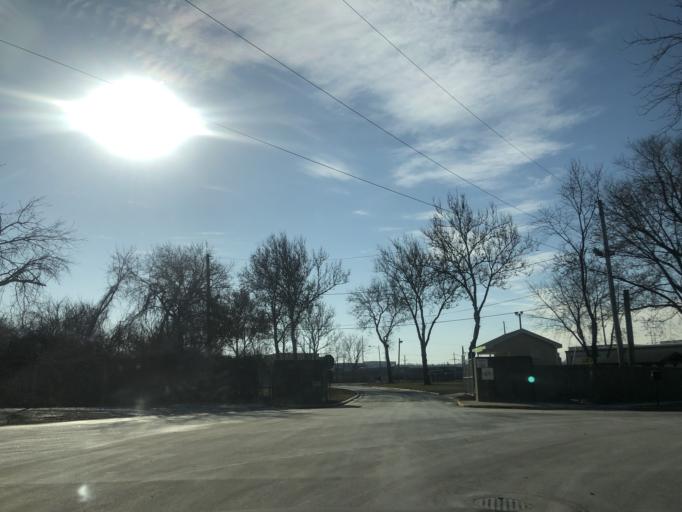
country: US
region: Illinois
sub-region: Cook County
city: Stickney
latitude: 41.8145
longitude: -87.7825
